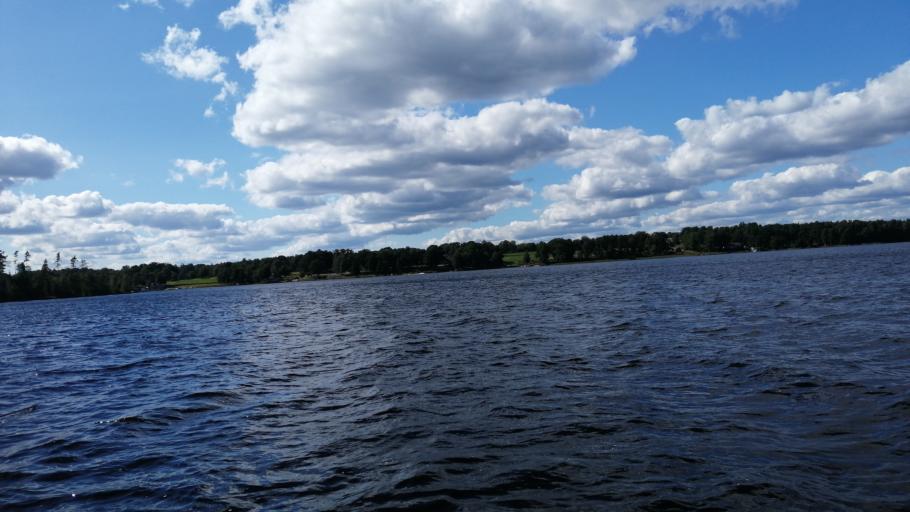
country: SE
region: Joenkoeping
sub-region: Varnamo Kommun
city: Bredaryd
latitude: 57.0075
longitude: 13.7123
